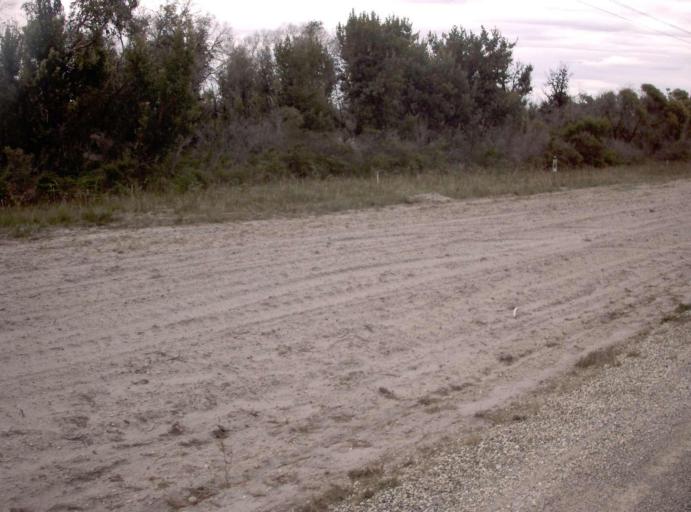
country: AU
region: Victoria
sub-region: East Gippsland
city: Bairnsdale
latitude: -38.1007
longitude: 147.5043
